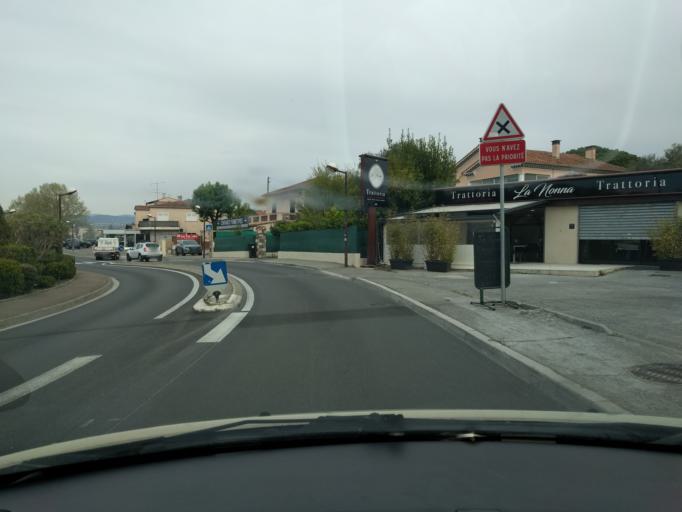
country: FR
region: Provence-Alpes-Cote d'Azur
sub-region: Departement des Alpes-Maritimes
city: La Roquette-sur-Siagne
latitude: 43.5770
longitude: 6.9522
